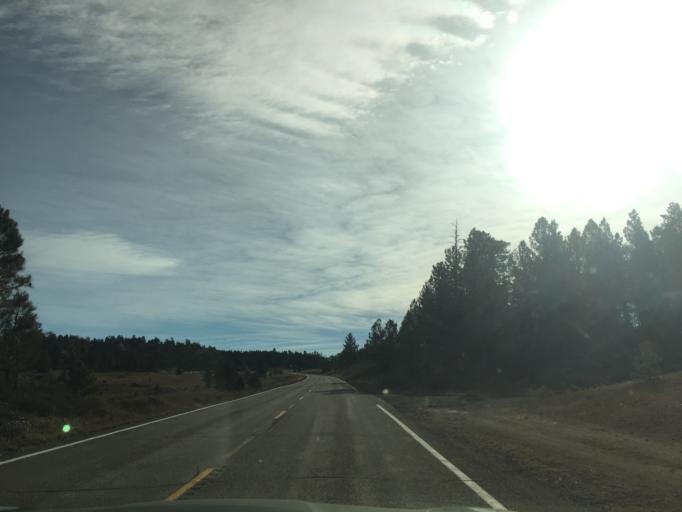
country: US
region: Utah
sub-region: Garfield County
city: Panguitch
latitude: 37.4972
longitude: -112.5864
